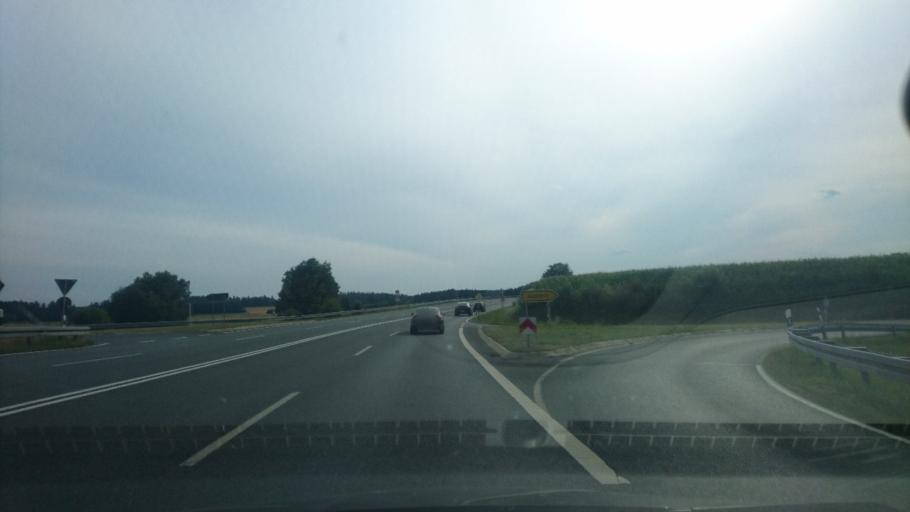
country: DE
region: Bavaria
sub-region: Upper Franconia
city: Koditz
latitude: 50.3047
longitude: 11.8550
